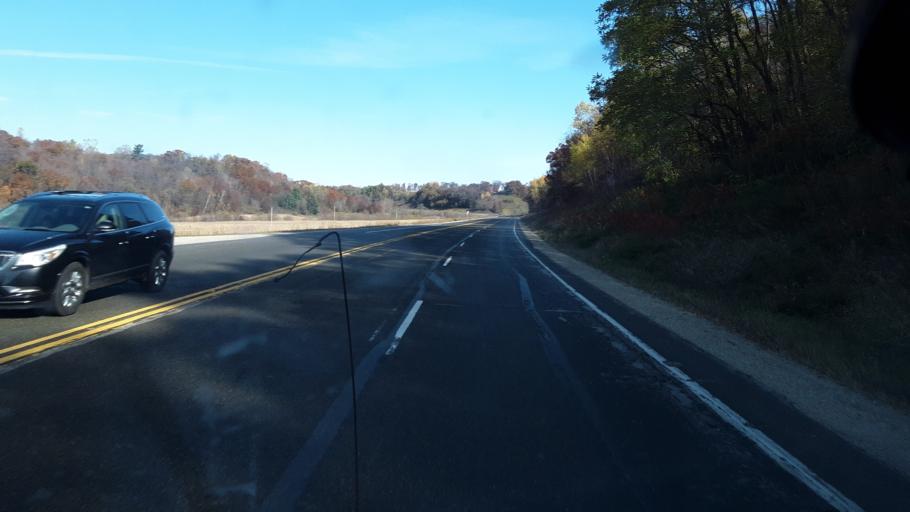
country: US
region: Wisconsin
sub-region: Monroe County
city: Tomah
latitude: 43.8792
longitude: -90.4812
